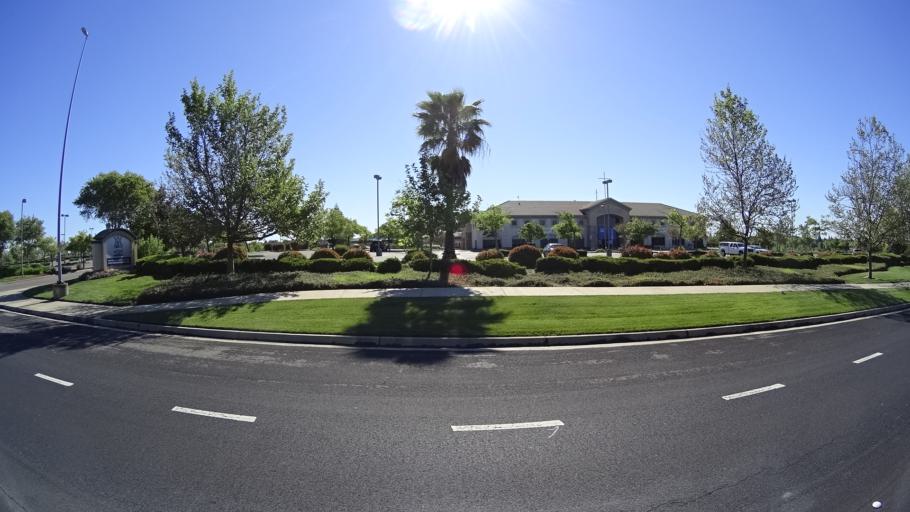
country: US
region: California
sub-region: Placer County
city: Rocklin
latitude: 38.7912
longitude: -121.2693
